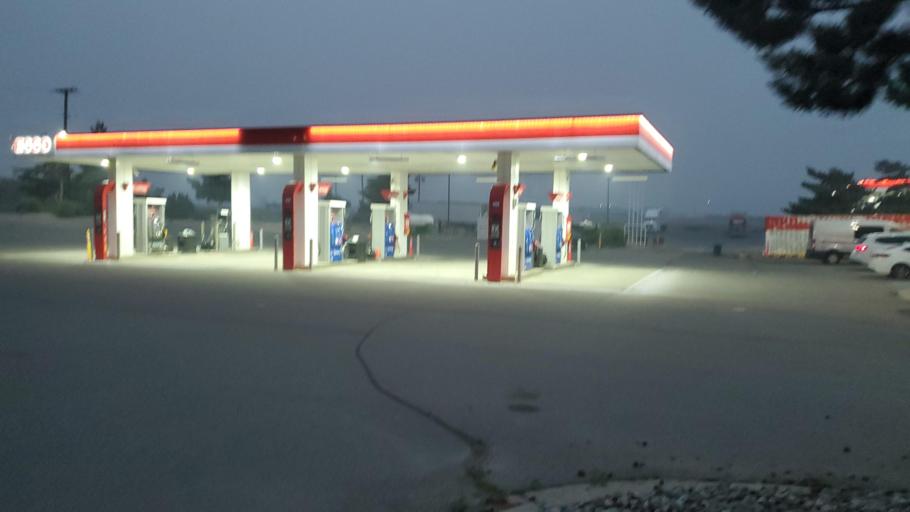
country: CA
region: British Columbia
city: Merritt
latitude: 50.1243
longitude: -120.7491
